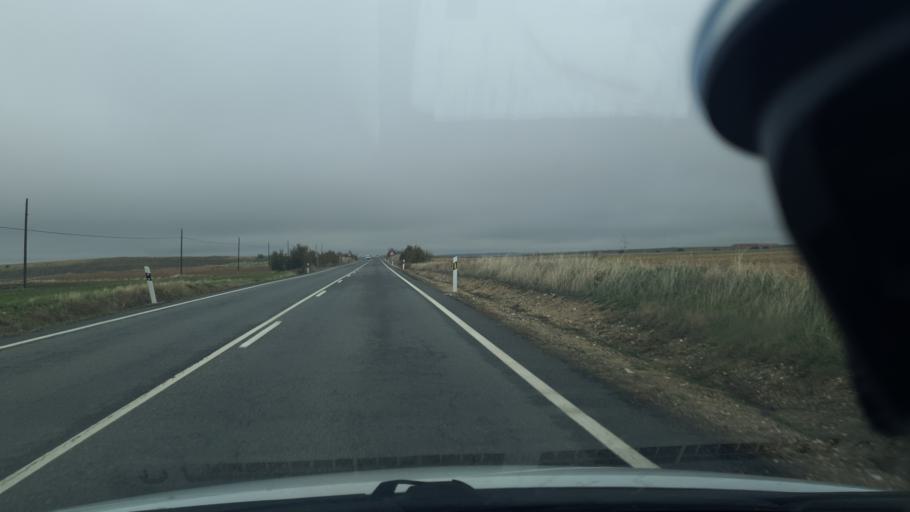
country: ES
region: Castille and Leon
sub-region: Provincia de Segovia
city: Encinillas
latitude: 41.0409
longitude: -4.1348
